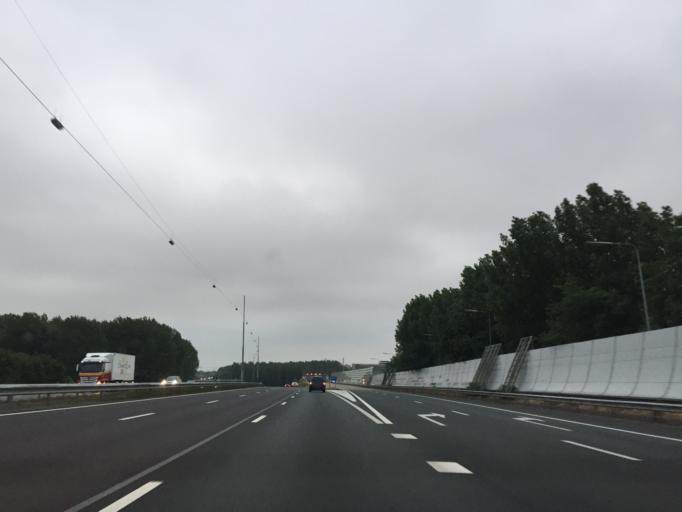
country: NL
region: North Holland
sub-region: Gemeente Landsmeer
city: Landsmeer
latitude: 52.4099
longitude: 4.9315
